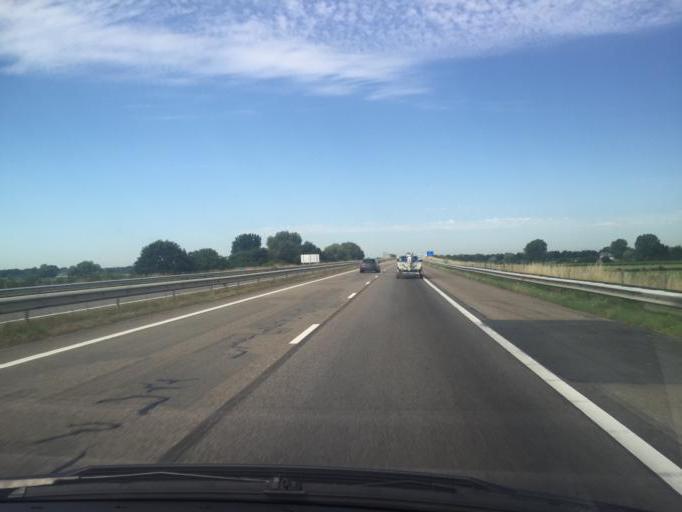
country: NL
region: North Brabant
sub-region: Gemeente Boxmeer
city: Boxmeer
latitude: 51.6647
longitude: 5.9742
